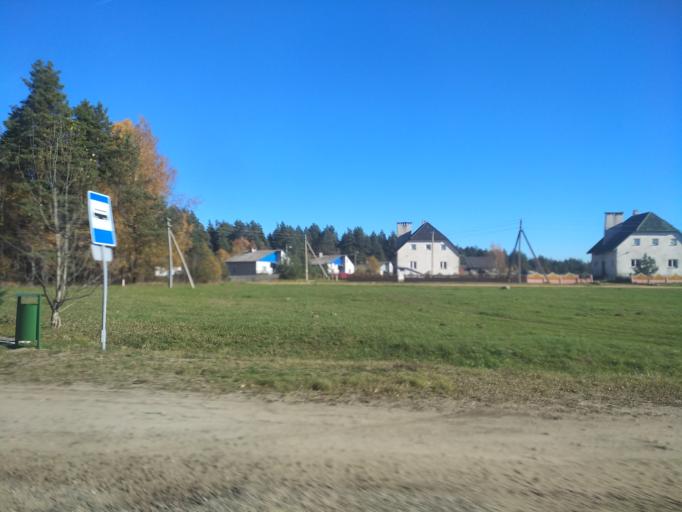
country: BY
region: Minsk
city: Kryvichy
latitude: 54.5719
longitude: 27.2043
